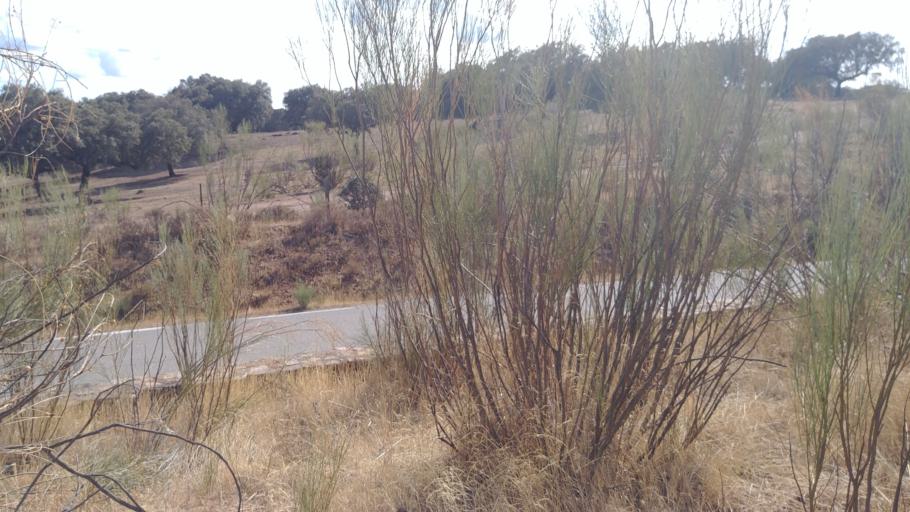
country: ES
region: Extremadura
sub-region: Provincia de Caceres
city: Torrejon el Rubio
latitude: 39.8222
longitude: -6.0498
